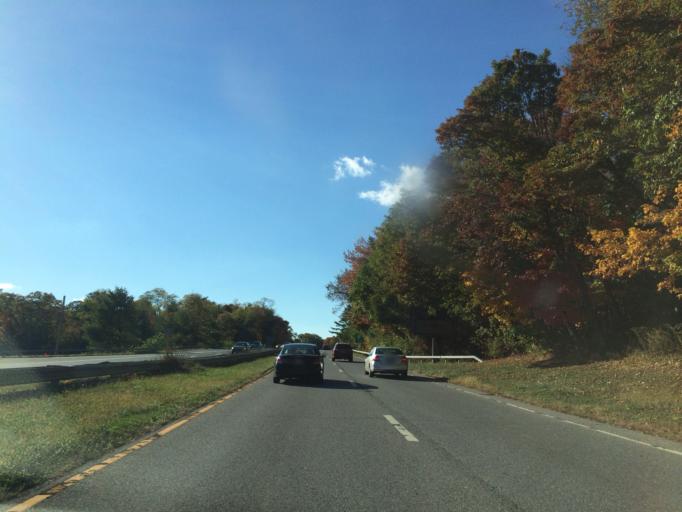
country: US
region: Connecticut
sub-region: Fairfield County
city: Westport
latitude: 41.1638
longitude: -73.3729
